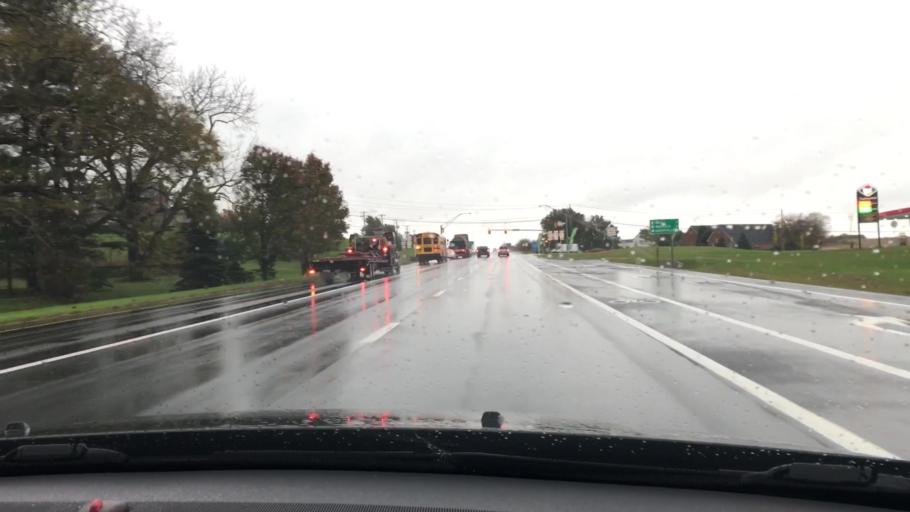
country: US
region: Pennsylvania
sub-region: Lancaster County
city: Willow Street
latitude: 39.9875
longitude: -76.2842
